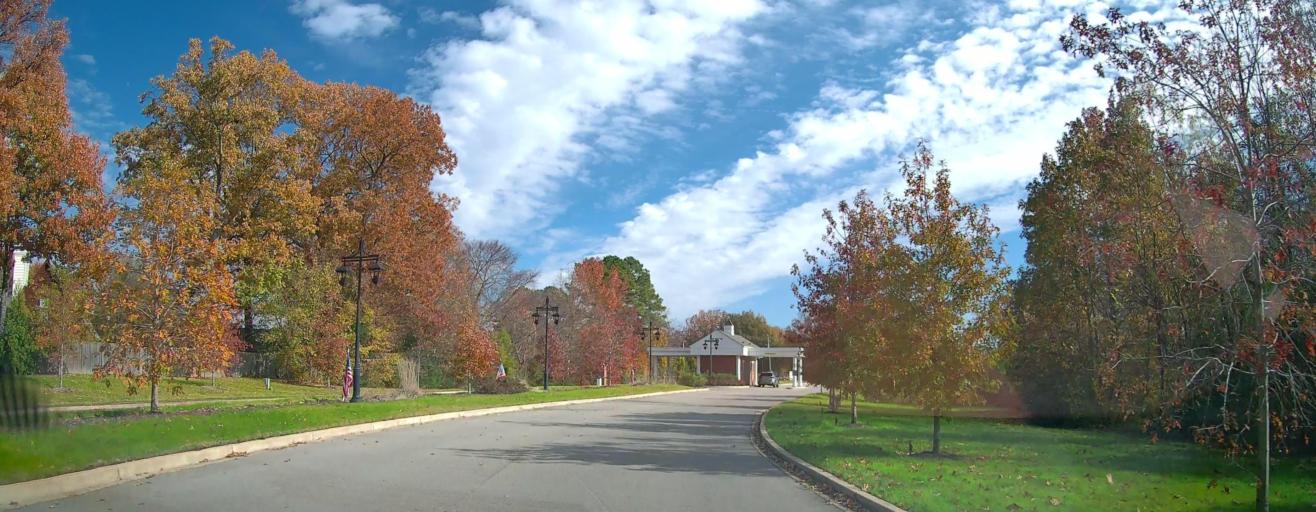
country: US
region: Tennessee
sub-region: Shelby County
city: Germantown
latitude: 35.0523
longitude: -89.8459
